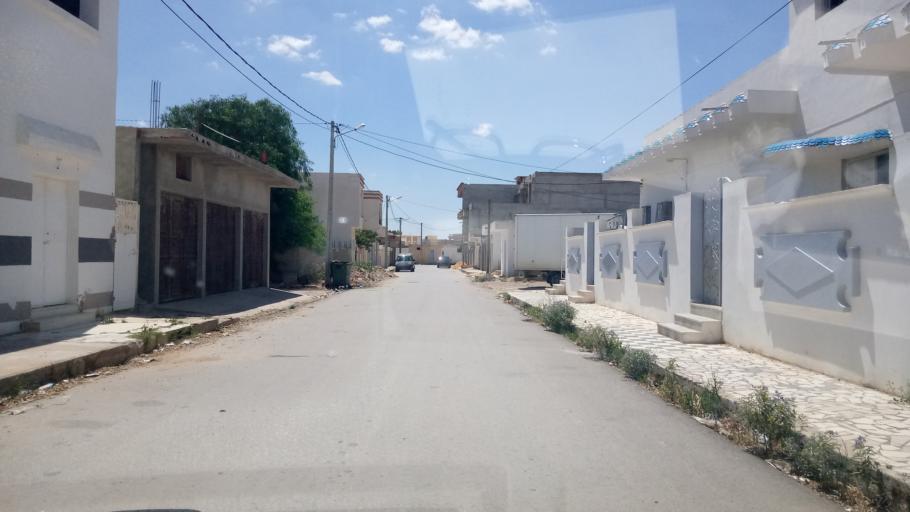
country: TN
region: Al Qayrawan
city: Sbikha
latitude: 36.1273
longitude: 10.0906
